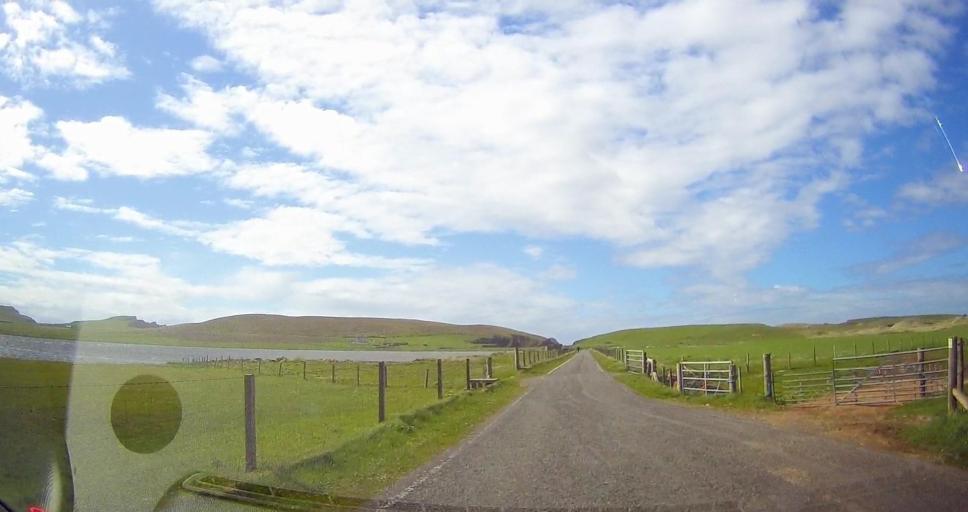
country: GB
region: Scotland
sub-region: Shetland Islands
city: Sandwick
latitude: 59.9416
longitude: -1.3320
